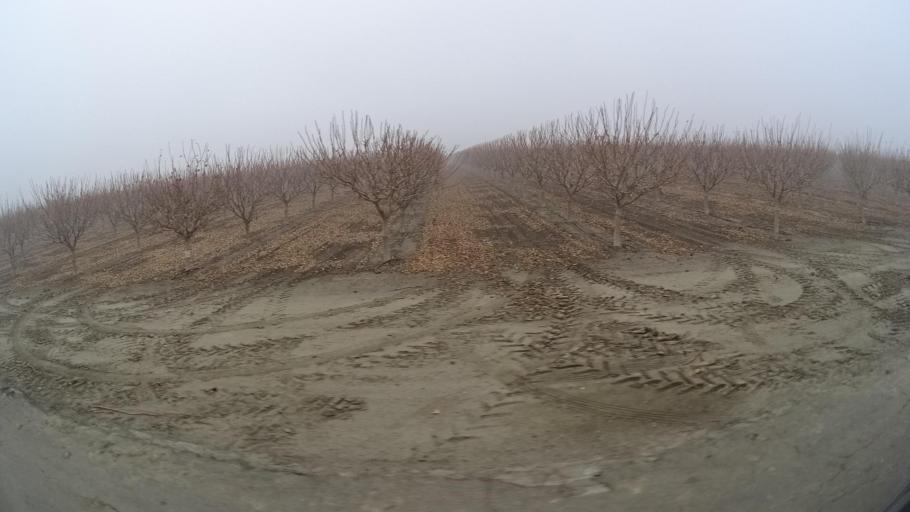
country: US
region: California
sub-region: Kern County
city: Buttonwillow
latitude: 35.4562
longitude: -119.5489
